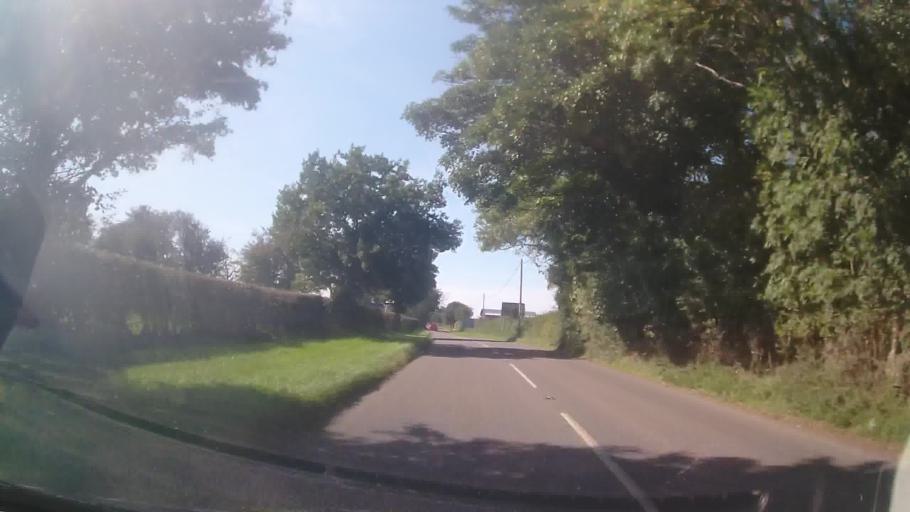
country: GB
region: Wales
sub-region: Sir Powys
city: Montgomery
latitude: 52.5314
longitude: -3.1081
